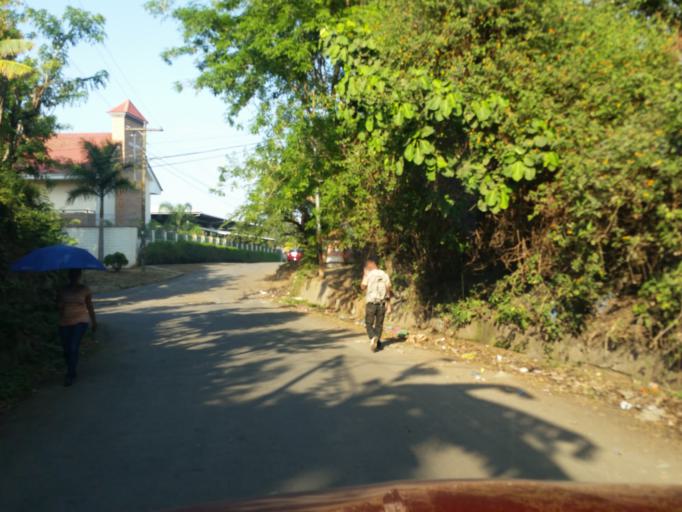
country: NI
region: Managua
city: Managua
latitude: 12.0816
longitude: -86.2332
